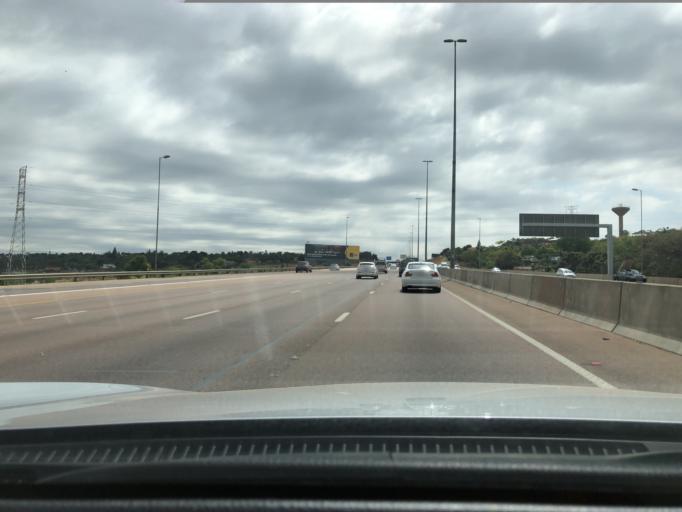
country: ZA
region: Gauteng
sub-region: City of Tshwane Metropolitan Municipality
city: Centurion
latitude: -25.8256
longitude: 28.2473
